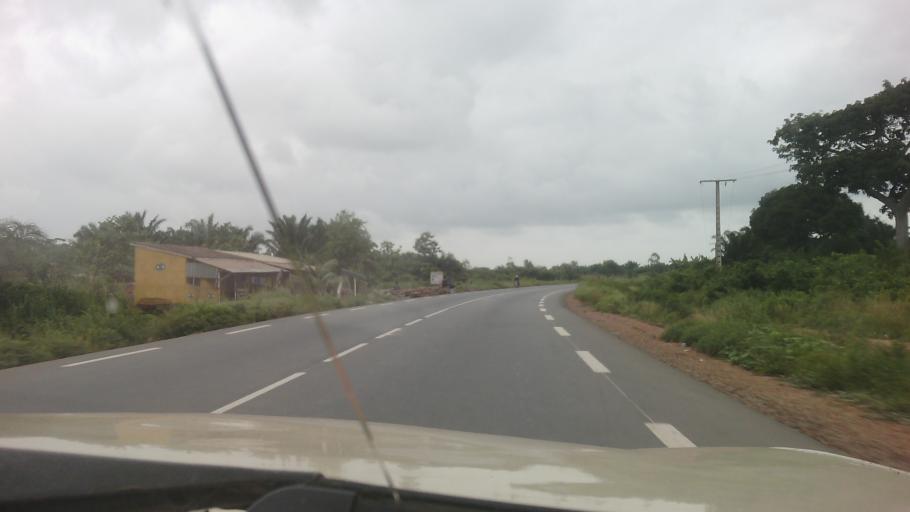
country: BJ
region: Atlantique
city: Ouidah
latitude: 6.3851
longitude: 2.0146
